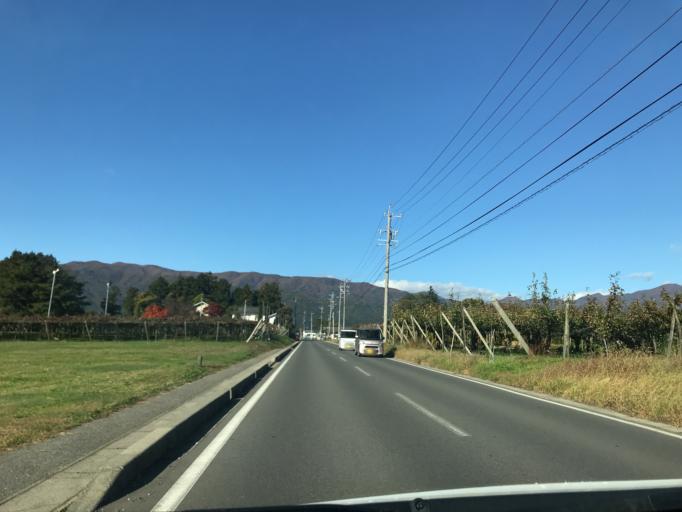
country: JP
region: Nagano
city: Shiojiri
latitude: 36.1579
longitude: 137.8971
